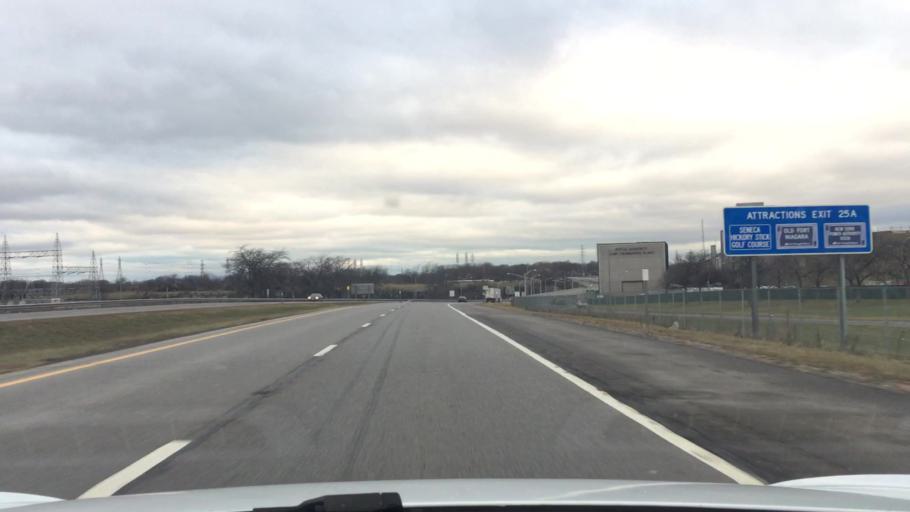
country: US
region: New York
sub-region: Niagara County
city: Lewiston
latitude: 43.1378
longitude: -79.0215
